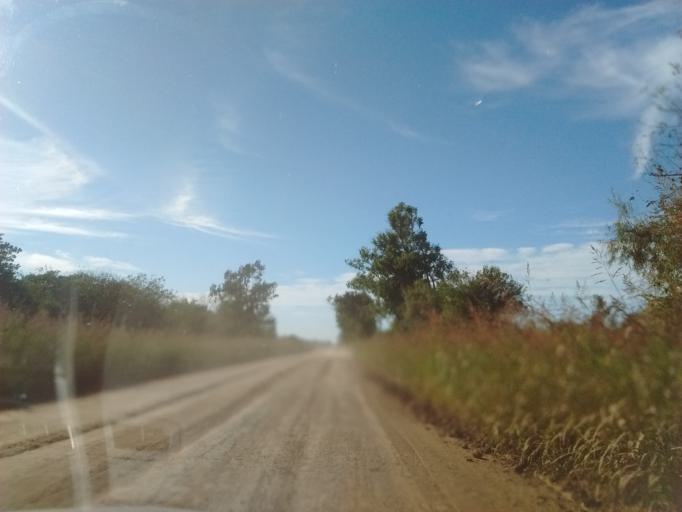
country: AR
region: Santa Fe
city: Coronda
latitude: -32.2299
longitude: -60.9706
